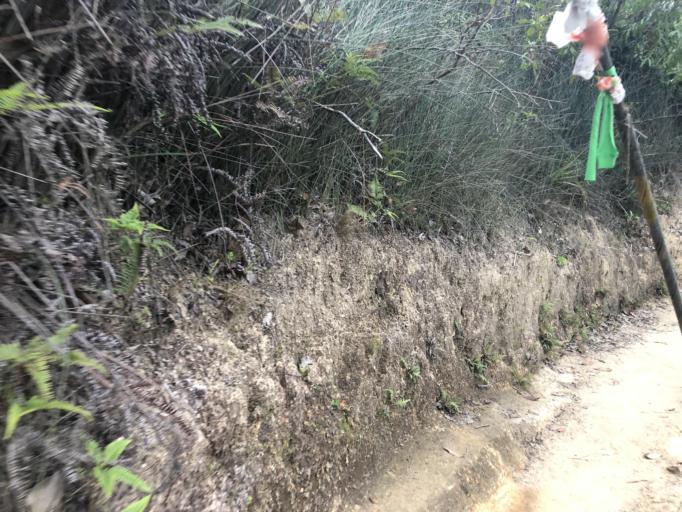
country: HK
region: Sha Tin
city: Sha Tin
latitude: 22.3924
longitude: 114.1752
